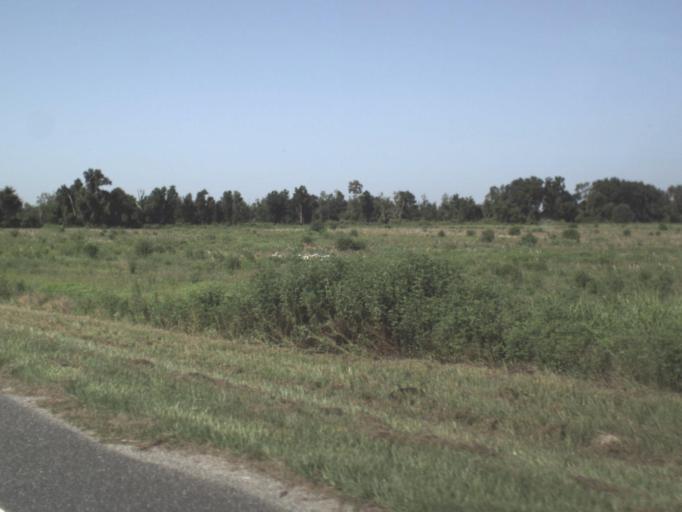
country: US
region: Florida
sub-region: Alachua County
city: High Springs
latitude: 29.9428
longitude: -82.7136
